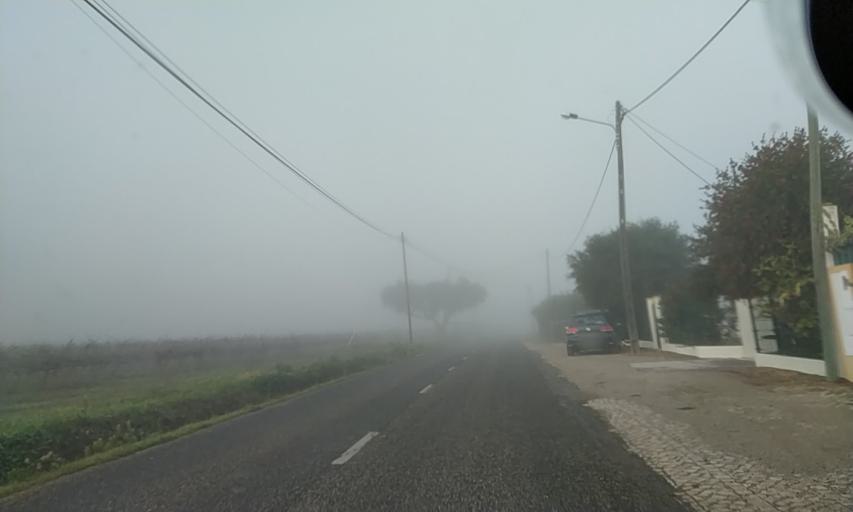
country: PT
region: Setubal
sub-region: Palmela
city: Palmela
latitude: 38.6079
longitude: -8.8589
